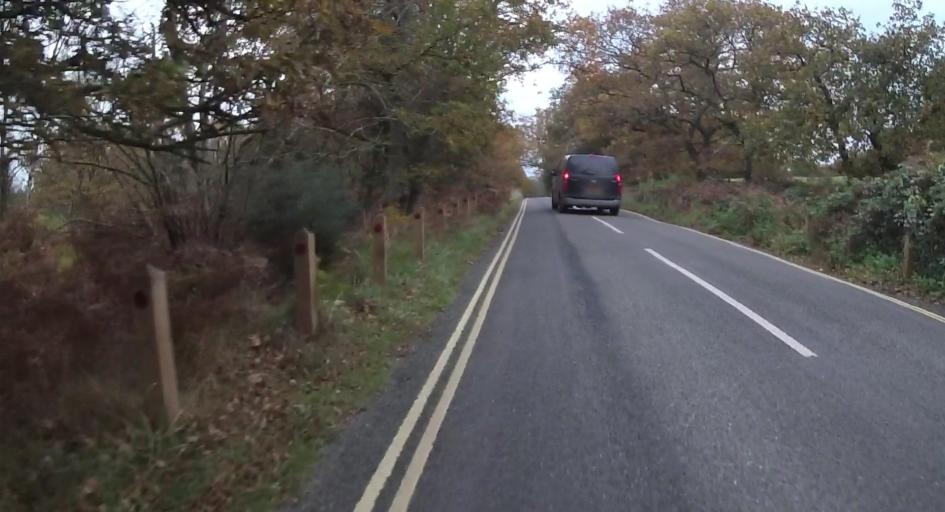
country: GB
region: England
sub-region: Surrey
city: Churt
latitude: 51.1566
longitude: -0.7969
